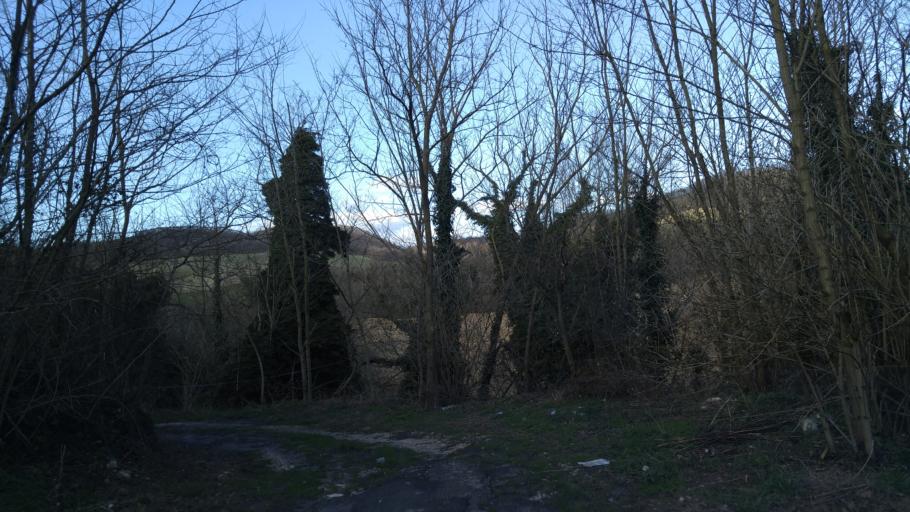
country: IT
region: The Marches
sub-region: Provincia di Pesaro e Urbino
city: Cagli
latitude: 43.5420
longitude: 12.6701
